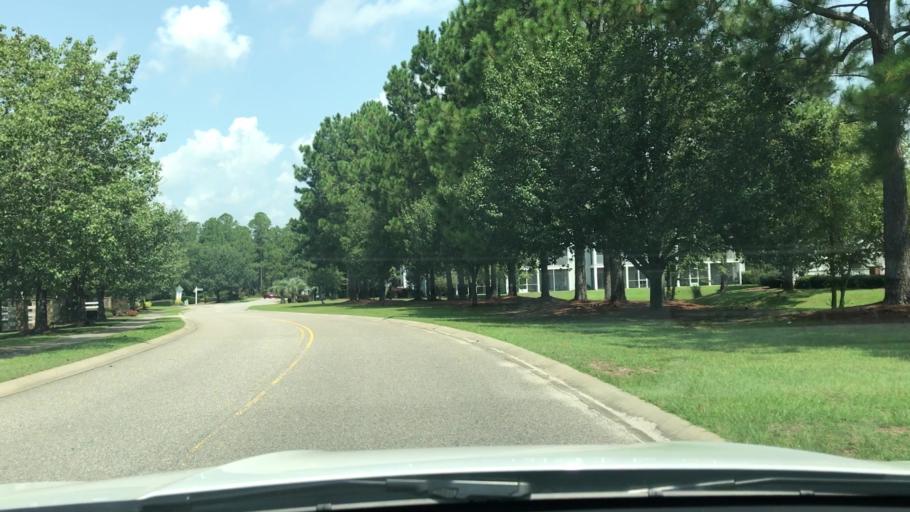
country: US
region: South Carolina
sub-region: Horry County
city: Forestbrook
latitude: 33.7804
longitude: -78.9657
